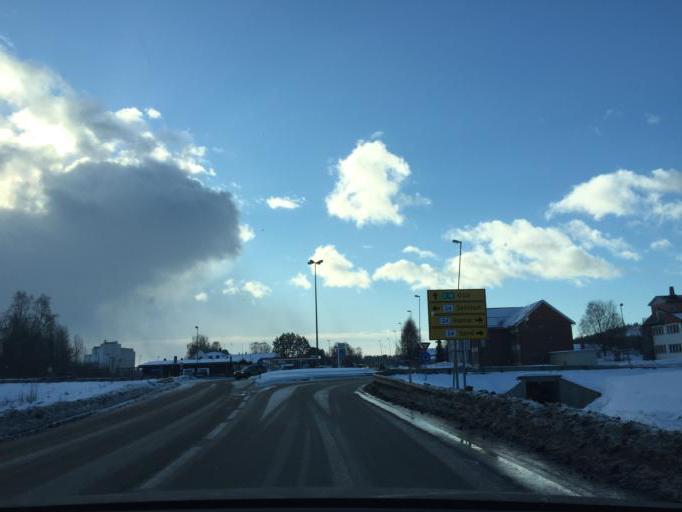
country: NO
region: Hedmark
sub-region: Sor-Odal
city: Skarnes
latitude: 60.2581
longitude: 11.6758
